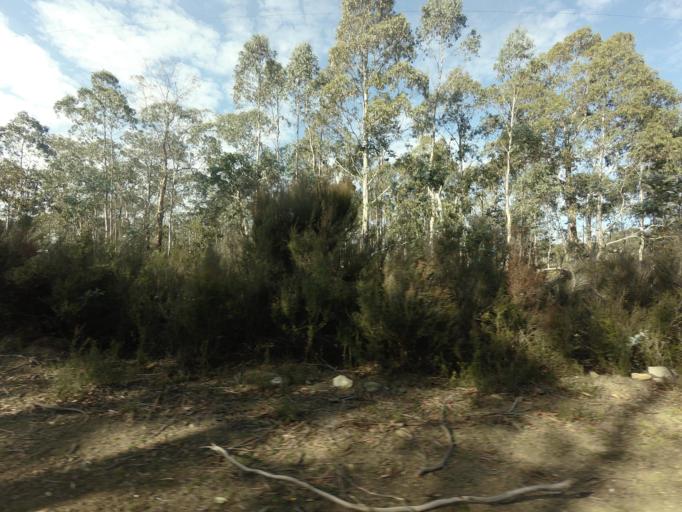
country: AU
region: Tasmania
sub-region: Sorell
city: Sorell
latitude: -42.5059
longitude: 147.4780
